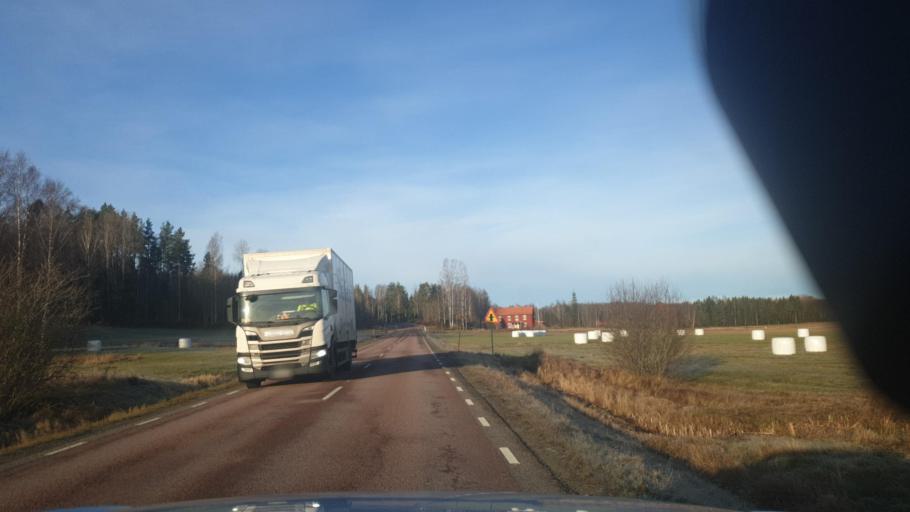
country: SE
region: Vaermland
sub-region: Grums Kommun
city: Grums
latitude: 59.4549
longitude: 12.9679
